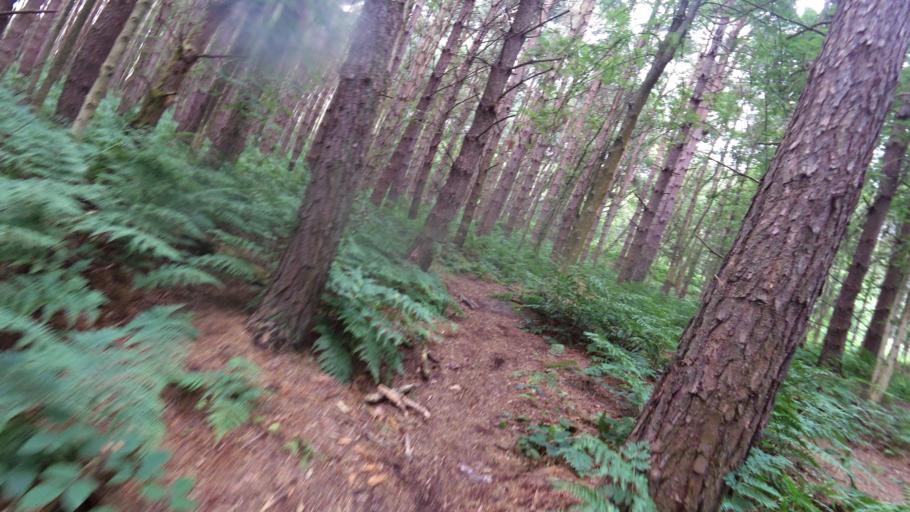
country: GB
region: England
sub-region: City and Borough of Leeds
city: Otley
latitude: 53.9558
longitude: -1.6830
